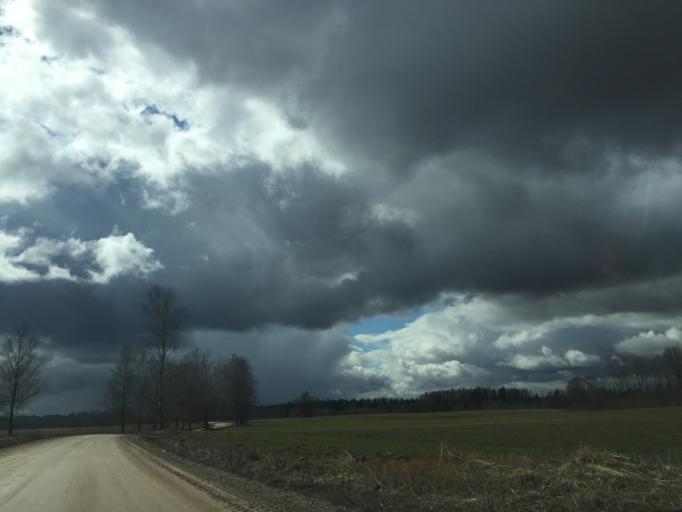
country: LV
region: Akniste
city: Akniste
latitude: 56.1144
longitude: 25.8861
